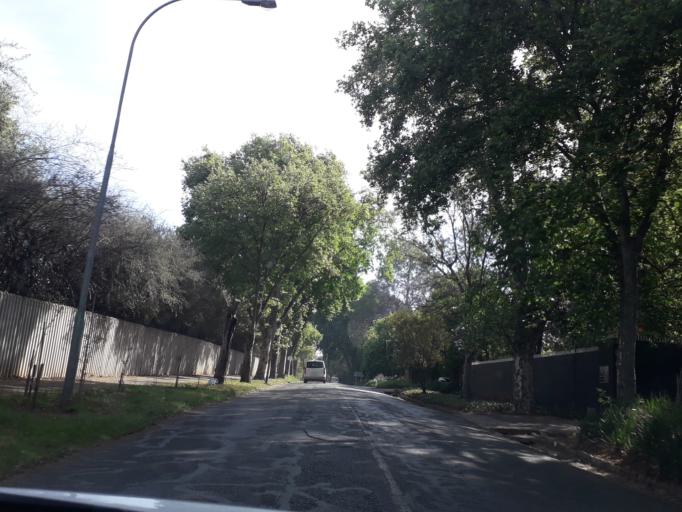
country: ZA
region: Gauteng
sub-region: City of Johannesburg Metropolitan Municipality
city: Johannesburg
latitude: -26.1667
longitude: 28.0416
